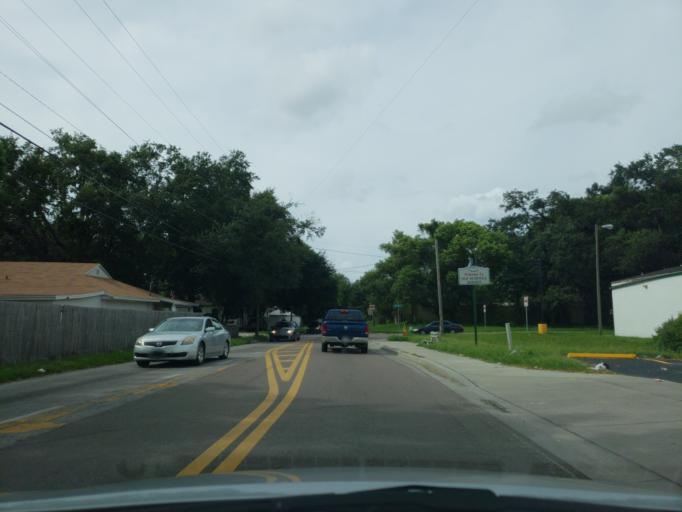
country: US
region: Florida
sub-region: Hillsborough County
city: Tampa
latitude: 27.9965
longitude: -82.4429
